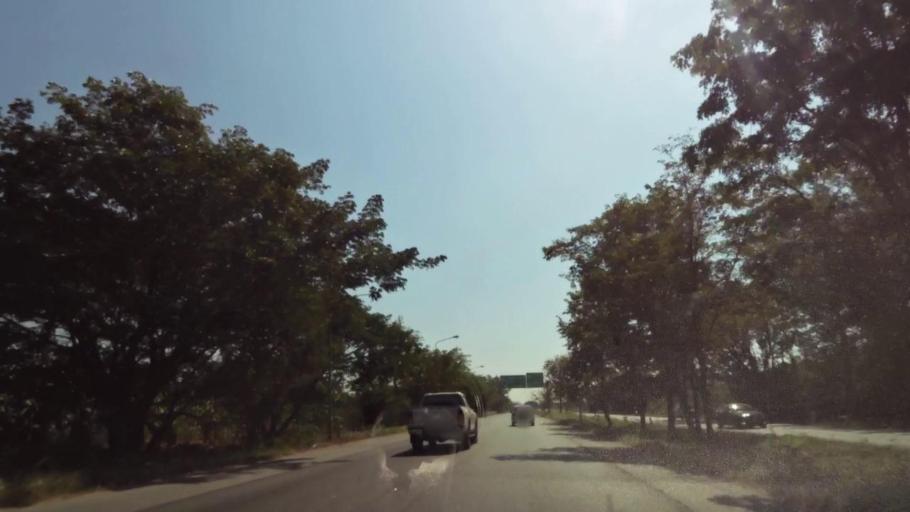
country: TH
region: Nakhon Sawan
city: Kao Liao
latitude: 15.8672
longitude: 100.1166
